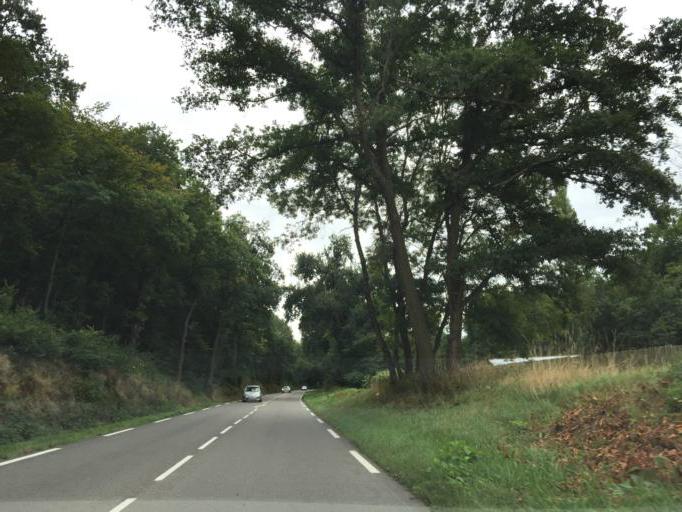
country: FR
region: Rhone-Alpes
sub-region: Departement de la Loire
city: La Talaudiere
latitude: 45.4725
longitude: 4.4124
